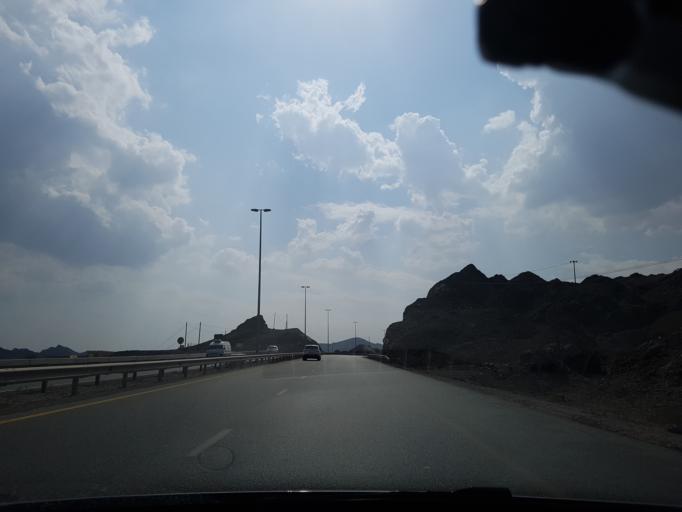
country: AE
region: Al Fujayrah
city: Dibba Al-Fujairah
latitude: 25.5263
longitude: 56.1155
